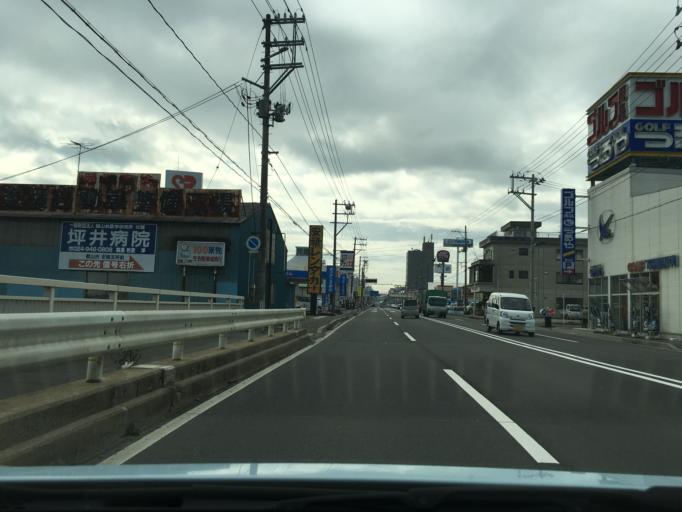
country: JP
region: Fukushima
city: Koriyama
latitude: 37.3642
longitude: 140.3691
